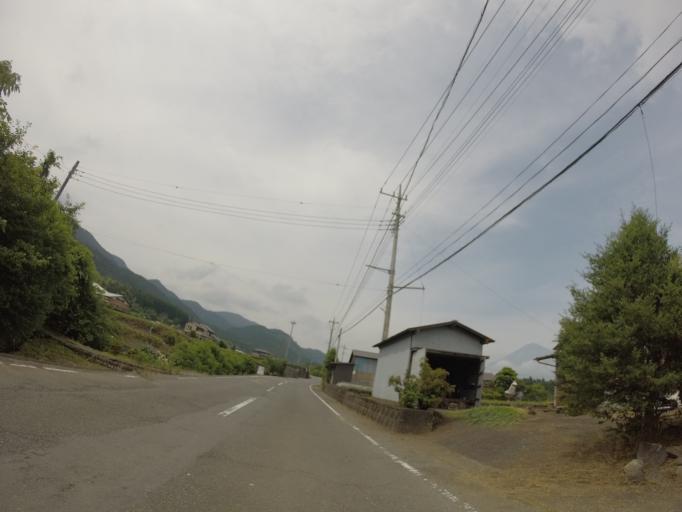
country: JP
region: Shizuoka
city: Fujinomiya
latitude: 35.2617
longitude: 138.5555
